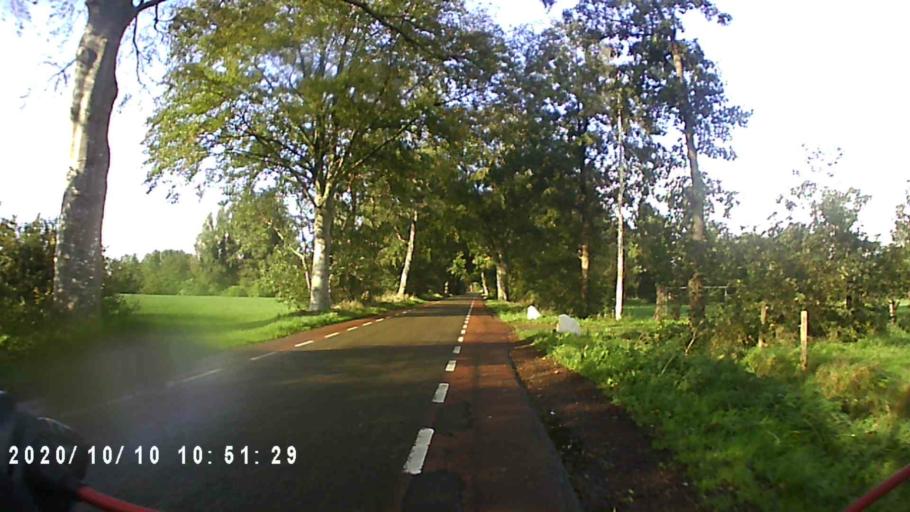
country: NL
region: Friesland
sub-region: Gemeente Achtkarspelen
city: Surhuisterveen
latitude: 53.1590
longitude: 6.2287
